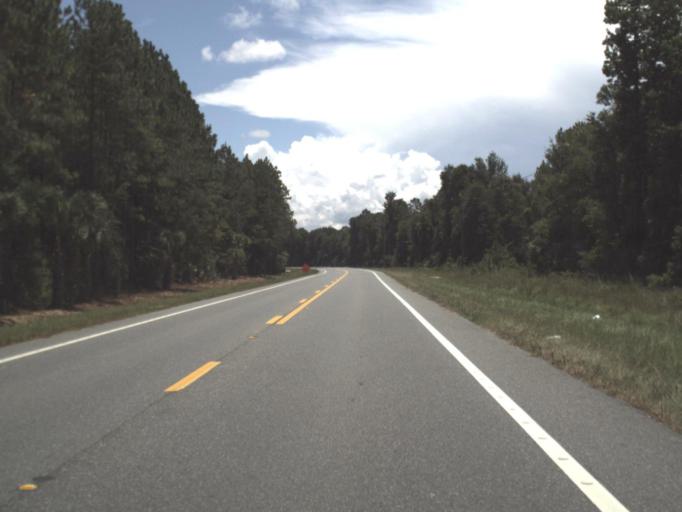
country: US
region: Florida
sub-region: Taylor County
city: Perry
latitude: 30.1420
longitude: -83.9347
